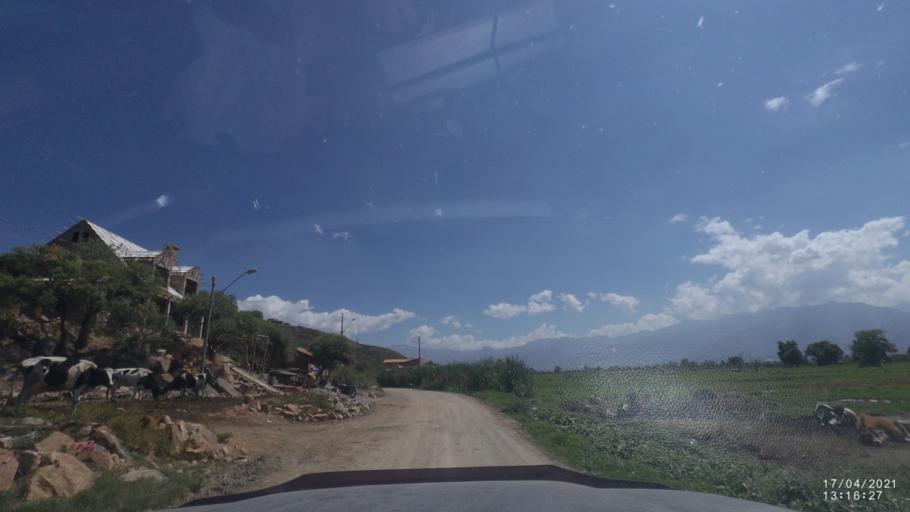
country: BO
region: Cochabamba
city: Cochabamba
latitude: -17.4166
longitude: -66.2369
